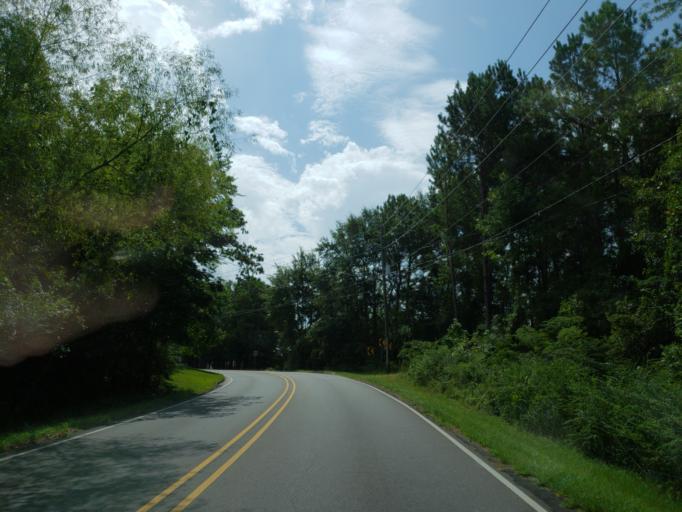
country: US
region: Mississippi
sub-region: Lamar County
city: Arnold Line
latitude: 31.3363
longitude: -89.3510
